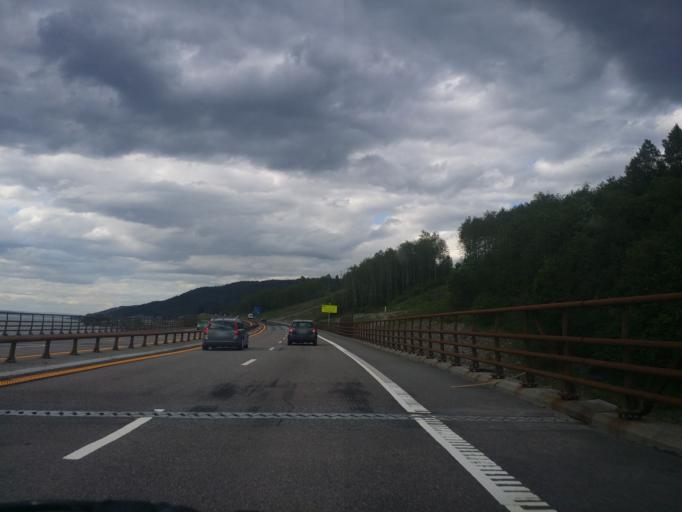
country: NO
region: Akershus
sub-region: Eidsvoll
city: Eidsvoll
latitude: 60.4024
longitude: 11.2363
